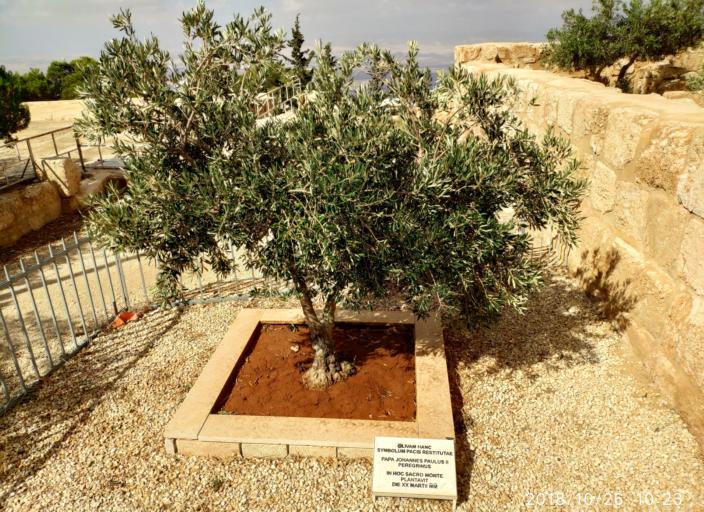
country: JO
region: Madaba
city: Madaba
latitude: 31.7680
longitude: 35.7253
